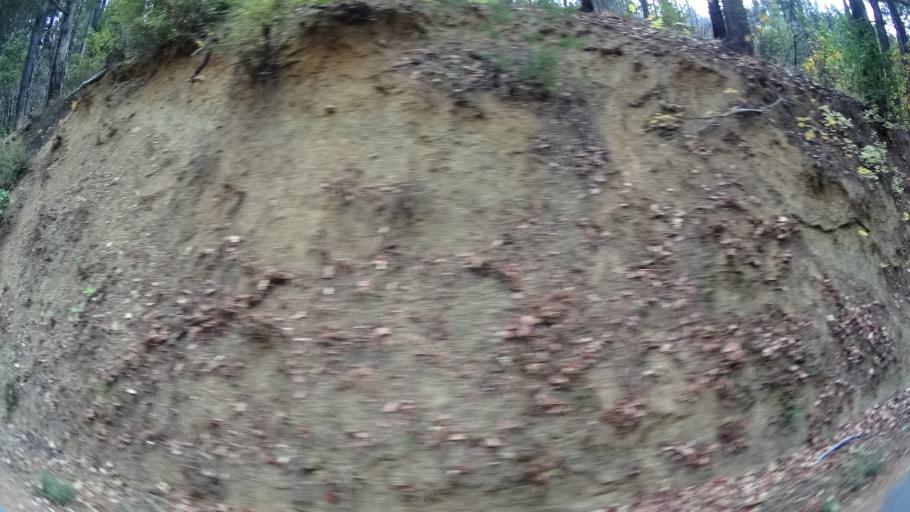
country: US
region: California
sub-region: Siskiyou County
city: Happy Camp
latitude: 41.7877
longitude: -123.3043
